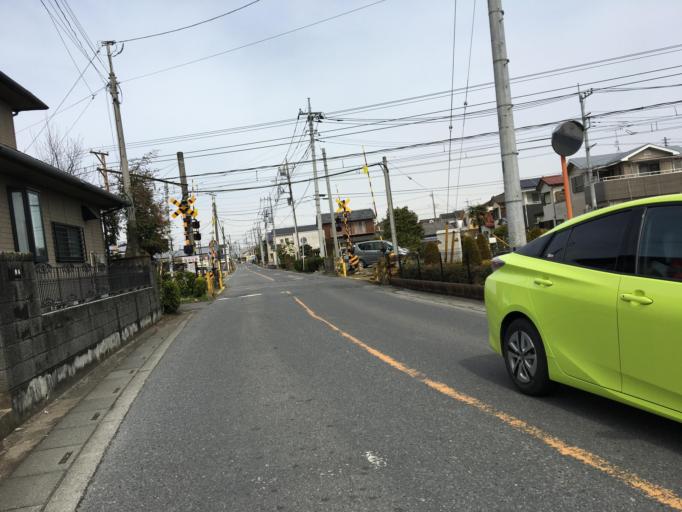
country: JP
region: Saitama
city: Yorii
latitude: 36.1286
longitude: 139.2201
